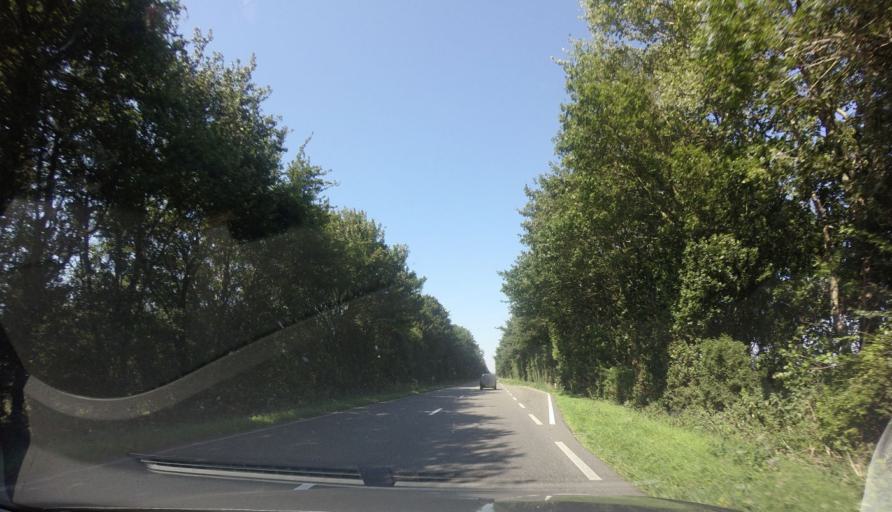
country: NL
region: North Holland
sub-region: Gemeente Langedijk
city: Broek op Langedijk
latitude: 52.6824
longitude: 4.7772
